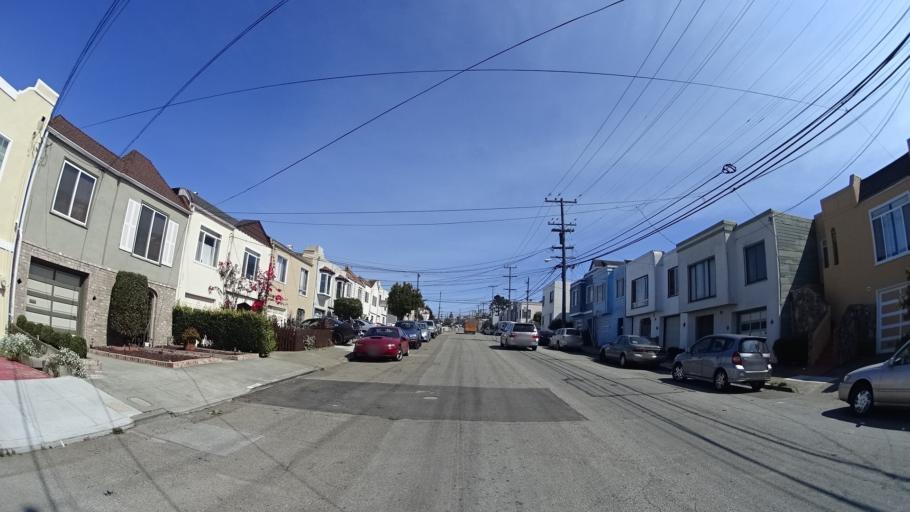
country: US
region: California
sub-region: San Mateo County
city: Daly City
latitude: 37.7197
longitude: -122.4679
